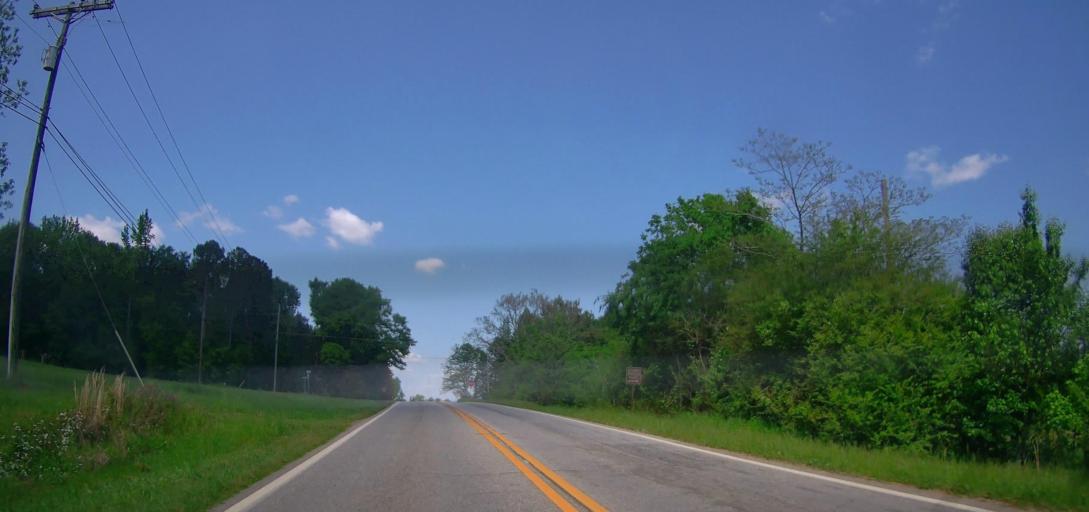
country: US
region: Georgia
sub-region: Putnam County
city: Eatonton
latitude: 33.3260
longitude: -83.2949
